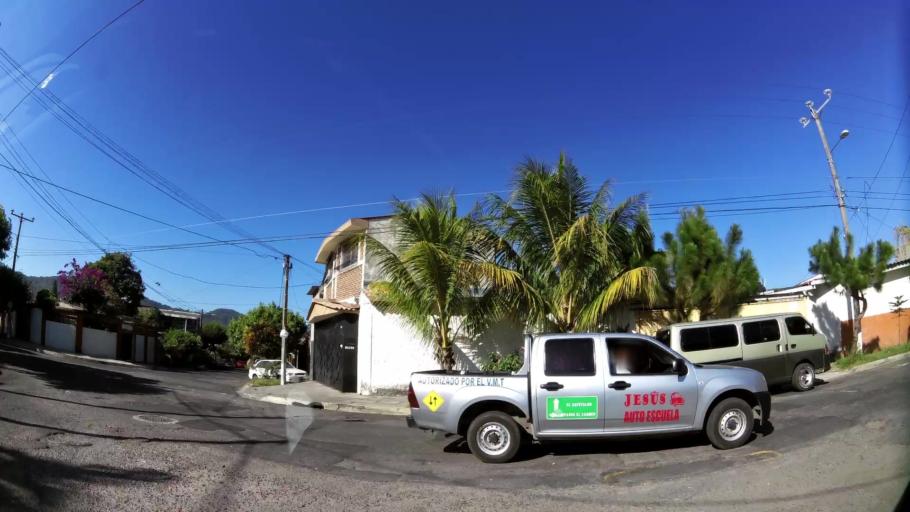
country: SV
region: La Libertad
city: Santa Tecla
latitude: 13.6829
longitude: -89.2944
